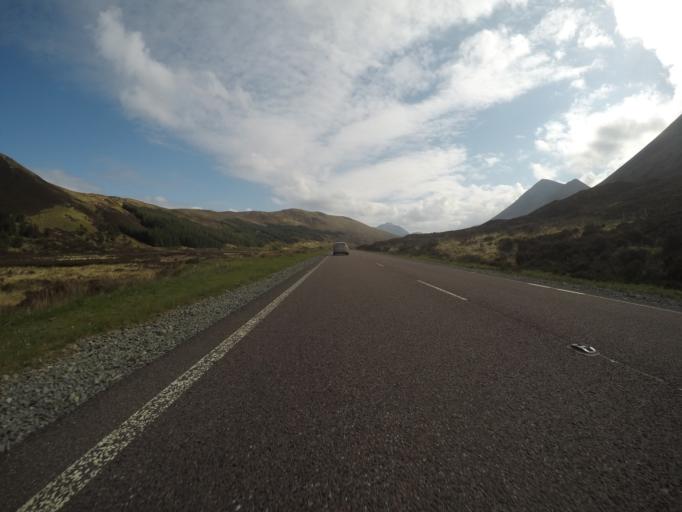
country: GB
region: Scotland
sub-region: Highland
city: Portree
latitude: 57.3034
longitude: -6.0904
